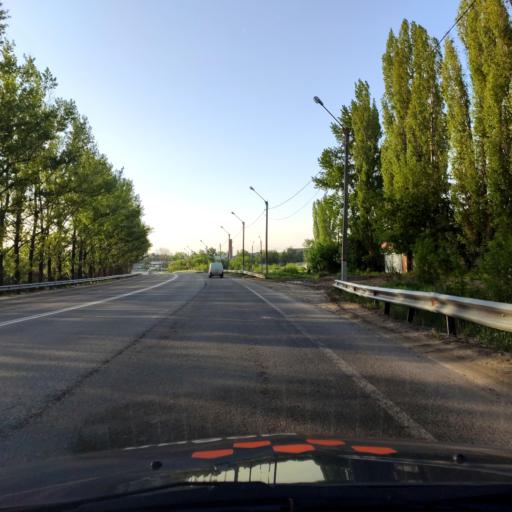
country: RU
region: Lipetsk
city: Yelets
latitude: 52.5983
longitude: 38.4750
